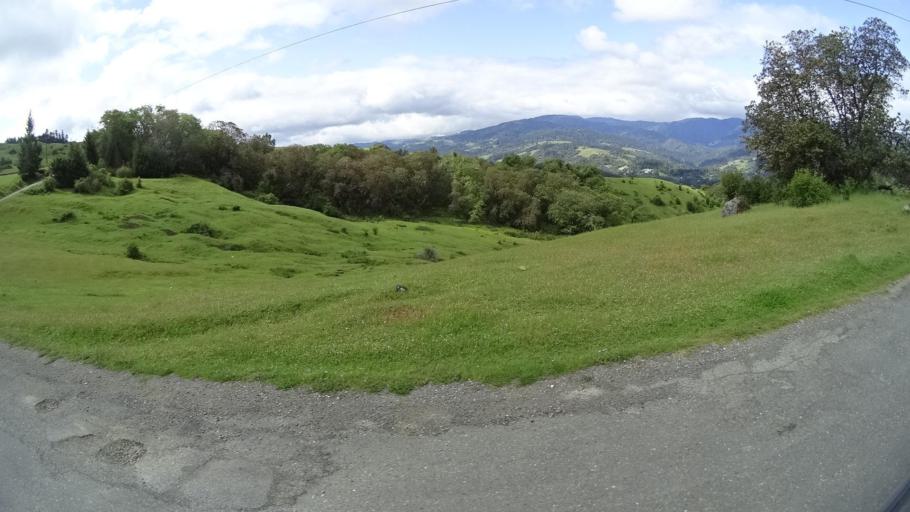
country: US
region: California
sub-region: Humboldt County
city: Redway
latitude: 40.1833
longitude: -123.5731
